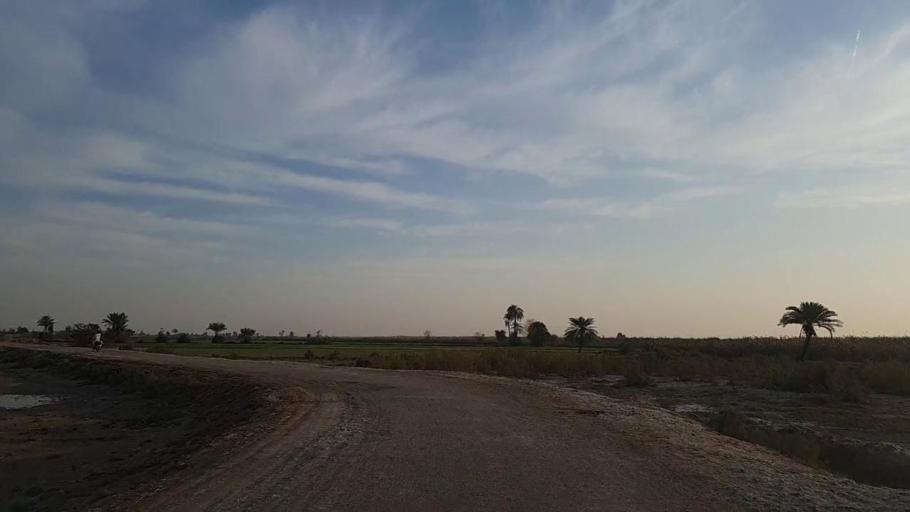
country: PK
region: Sindh
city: Bandhi
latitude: 26.5788
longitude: 68.3337
